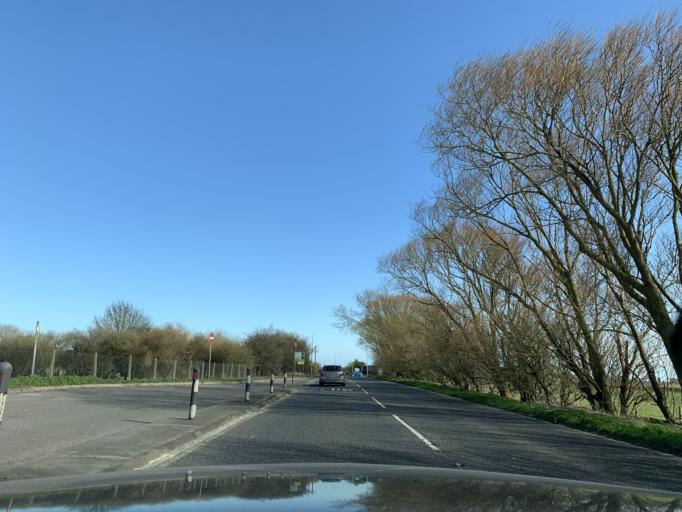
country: GB
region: England
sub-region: Kent
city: New Romney
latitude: 50.9853
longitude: 0.9195
